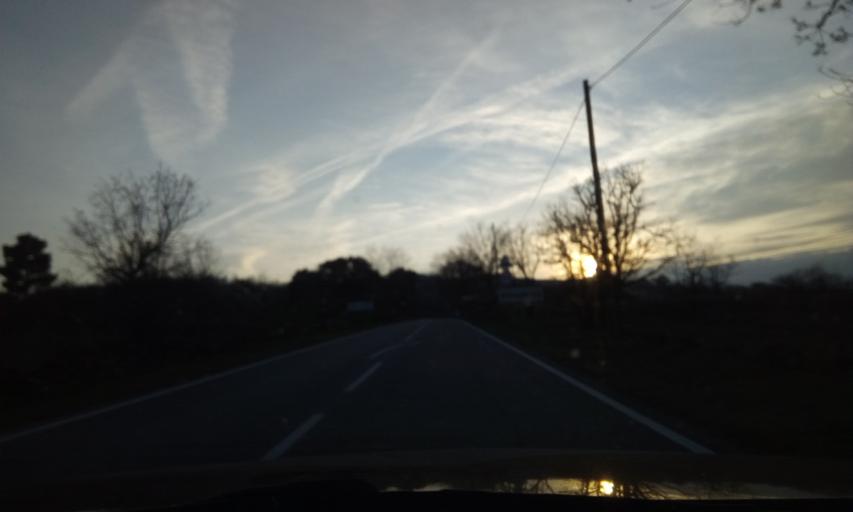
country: PT
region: Guarda
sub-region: Guarda
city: Sequeira
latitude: 40.5966
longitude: -7.1212
